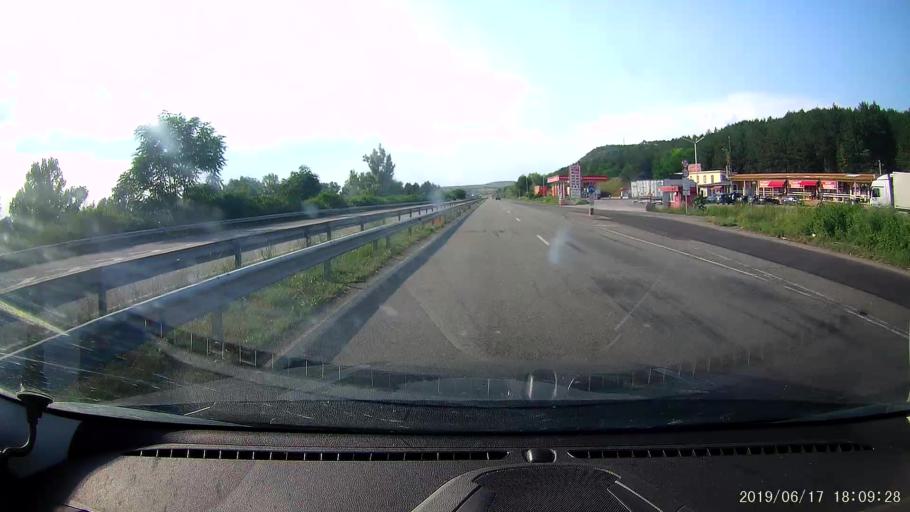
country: BG
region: Khaskovo
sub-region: Obshtina Lyubimets
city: Lyubimets
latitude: 41.8595
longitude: 26.0892
